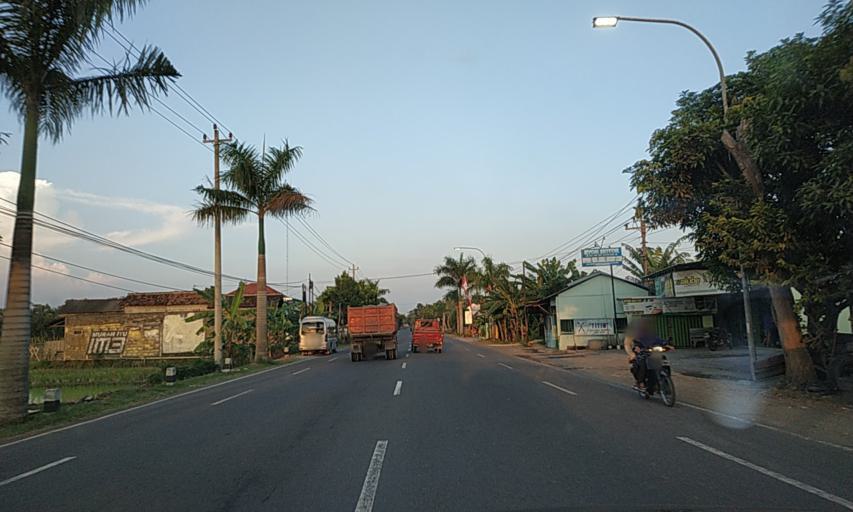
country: ID
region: Daerah Istimewa Yogyakarta
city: Srandakan
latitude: -7.8894
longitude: 110.1008
